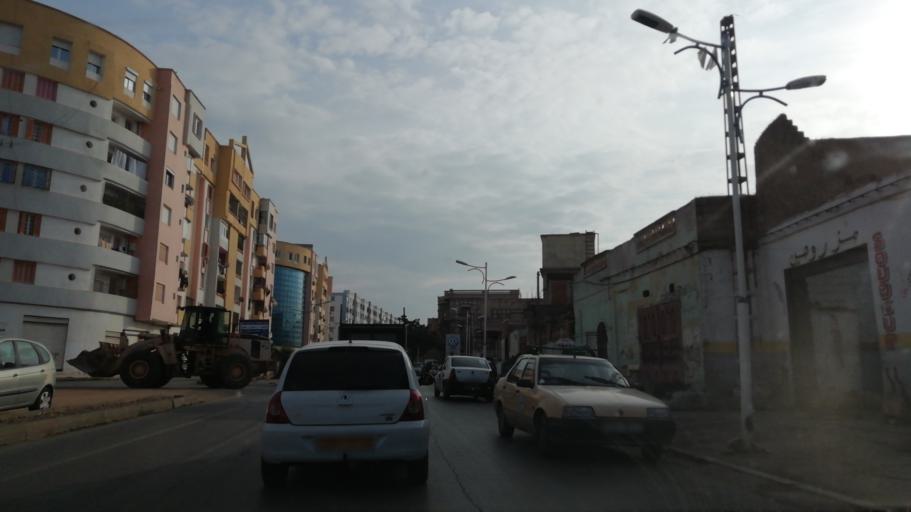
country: DZ
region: Mostaganem
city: Mostaganem
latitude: 35.8945
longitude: 0.0759
